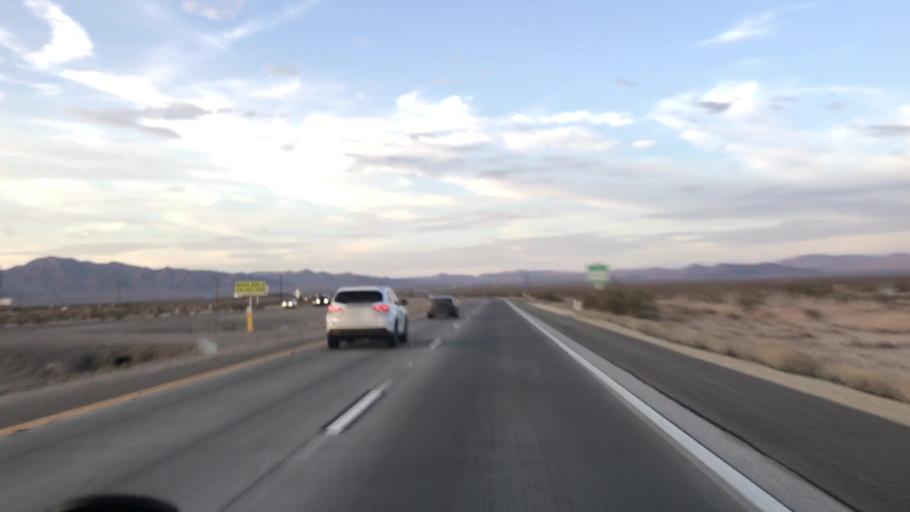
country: US
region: California
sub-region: San Bernardino County
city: Fort Irwin
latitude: 35.2752
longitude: -116.0542
